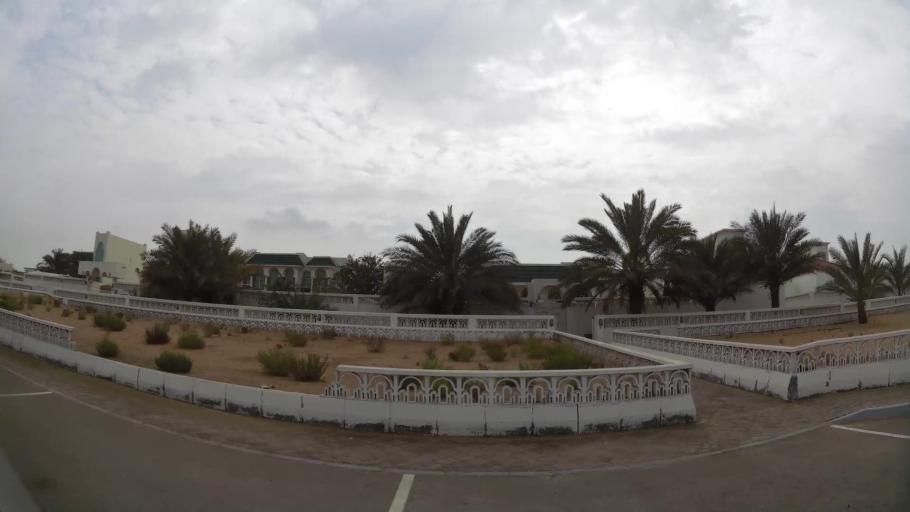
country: AE
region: Abu Dhabi
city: Abu Dhabi
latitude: 24.6291
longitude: 54.7103
